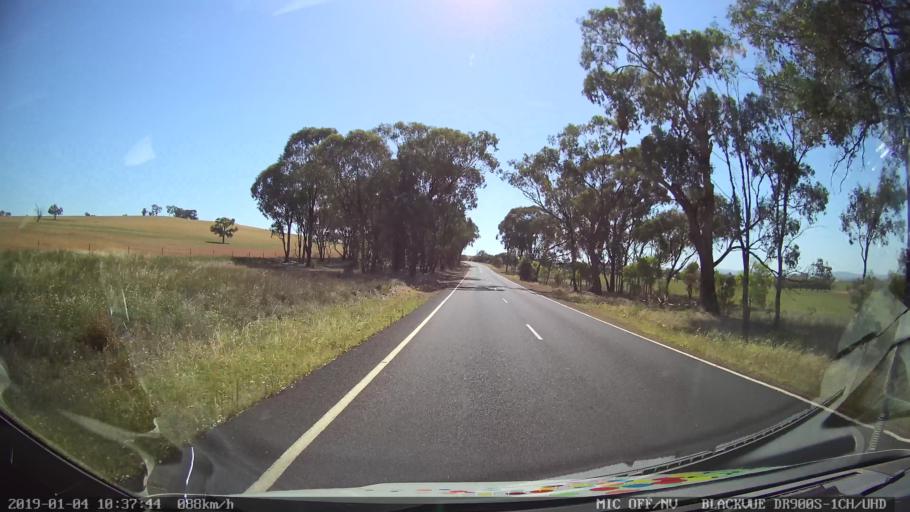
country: AU
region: New South Wales
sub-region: Cabonne
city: Molong
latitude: -33.2952
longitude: 148.6989
